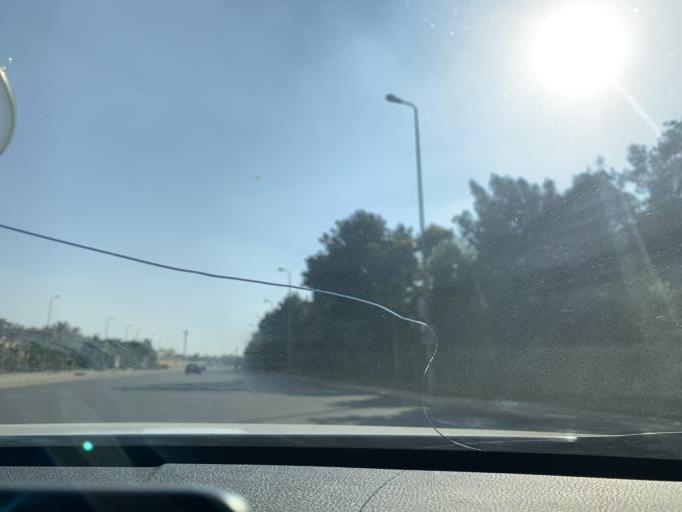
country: EG
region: Muhafazat al Qalyubiyah
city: Al Khankah
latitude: 30.0160
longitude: 31.4860
